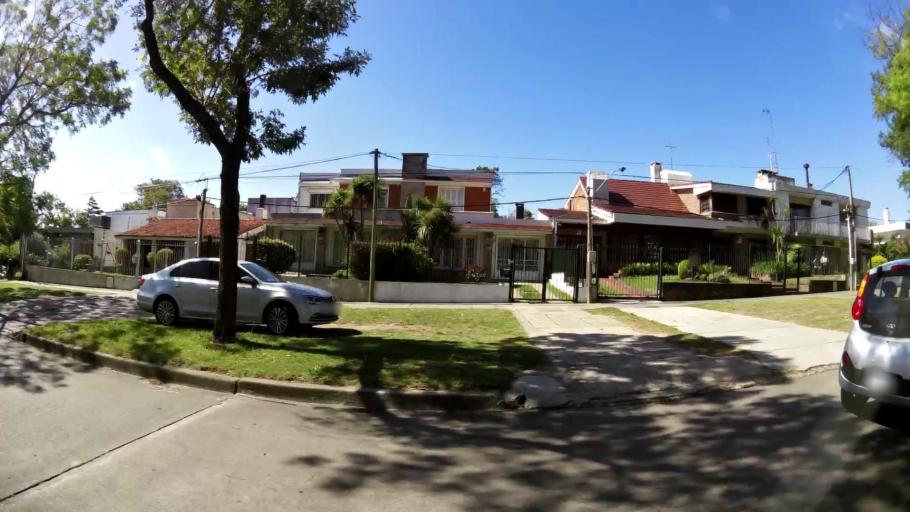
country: UY
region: Canelones
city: Paso de Carrasco
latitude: -34.8927
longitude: -56.0875
